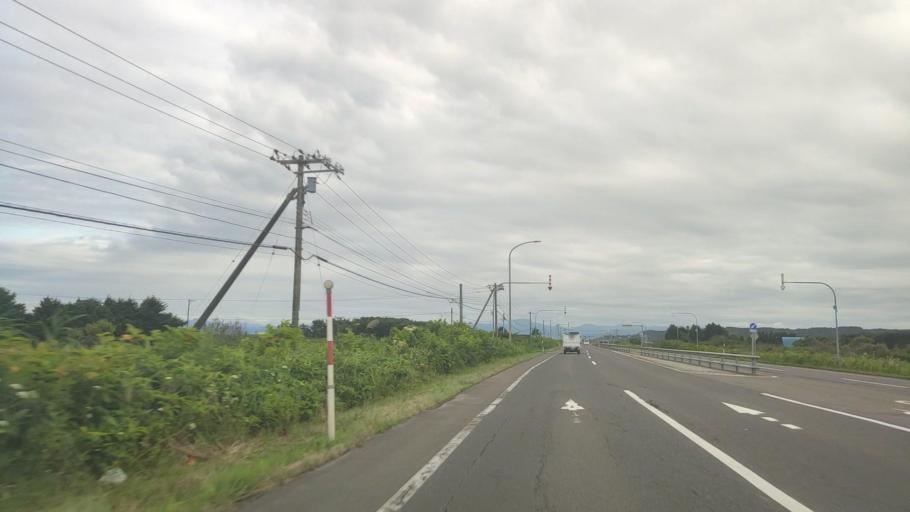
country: JP
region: Hokkaido
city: Niseko Town
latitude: 42.4088
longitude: 140.3063
